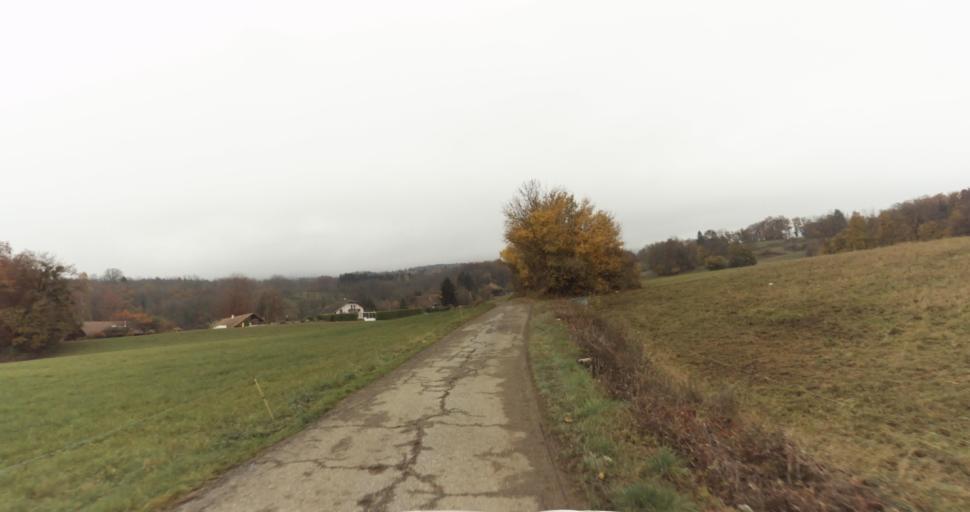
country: FR
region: Rhone-Alpes
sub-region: Departement de la Haute-Savoie
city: Cusy
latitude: 45.7534
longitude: 6.0134
